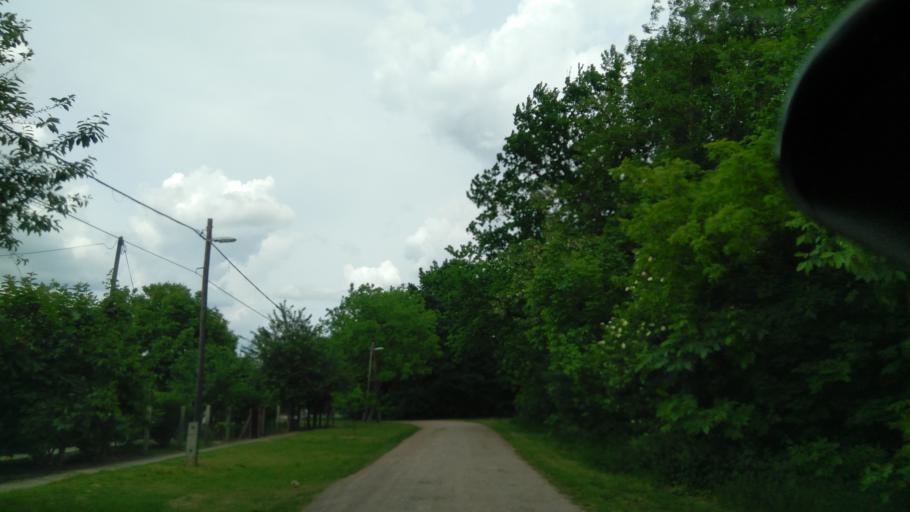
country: HU
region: Bekes
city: Mezohegyes
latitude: 46.3097
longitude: 20.8239
